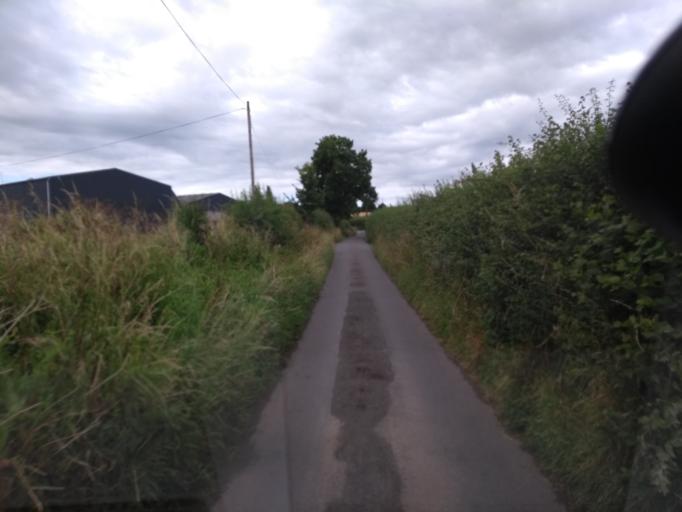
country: GB
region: England
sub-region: Somerset
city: Bridgwater
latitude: 51.1398
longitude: -3.0268
